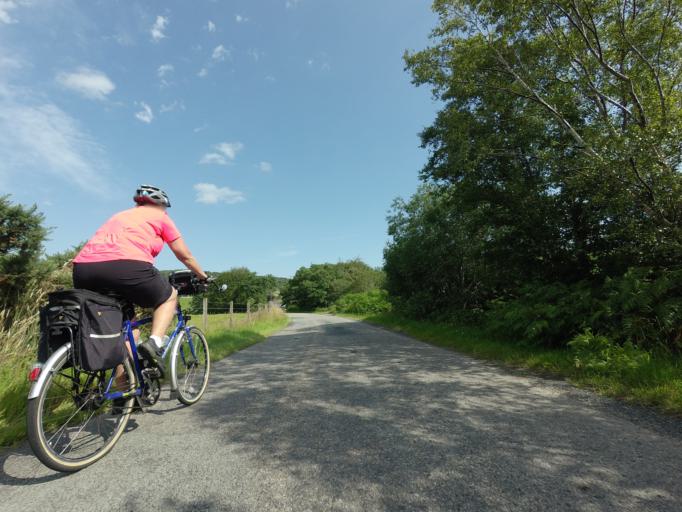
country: GB
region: Scotland
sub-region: Highland
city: Invergordon
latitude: 57.7508
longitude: -4.1603
